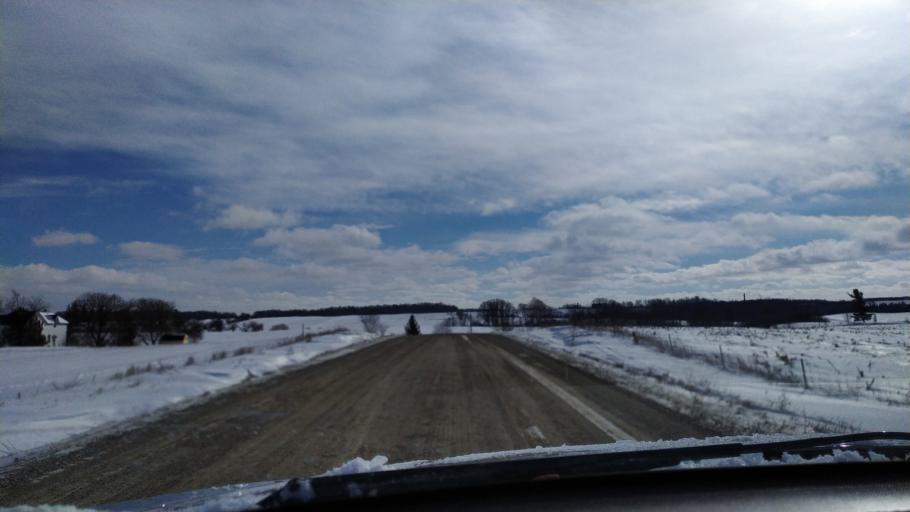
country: CA
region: Ontario
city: Waterloo
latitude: 43.4705
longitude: -80.7390
